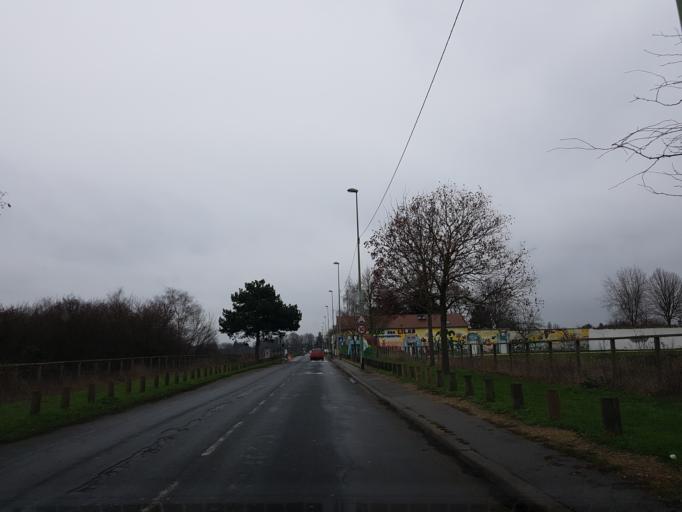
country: FR
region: Ile-de-France
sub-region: Departement du Val-de-Marne
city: Thiais
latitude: 48.7802
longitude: 2.3833
